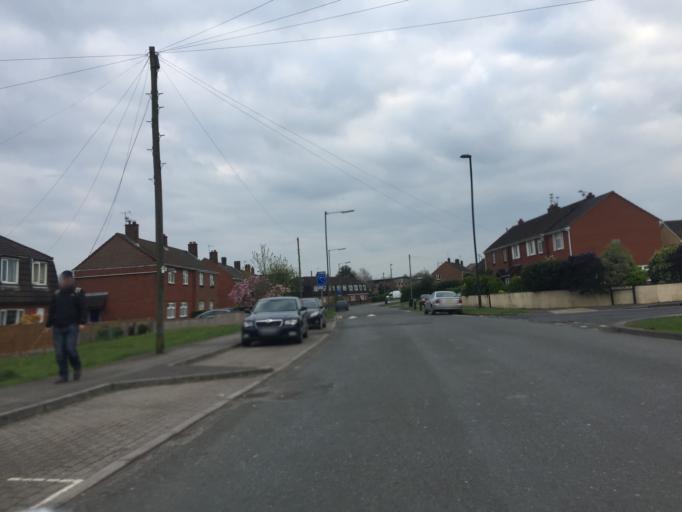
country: GB
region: England
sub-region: South Gloucestershire
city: Stoke Gifford
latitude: 51.5097
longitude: -2.5637
